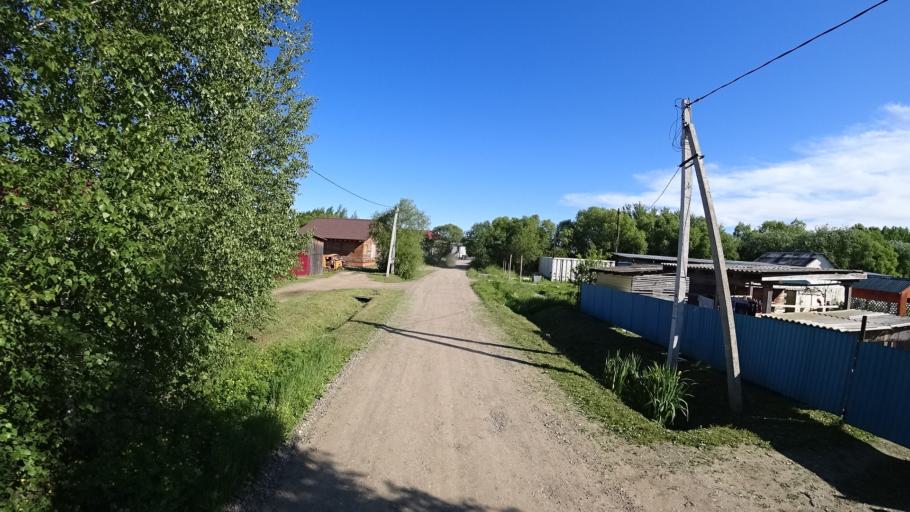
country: RU
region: Khabarovsk Krai
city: Khor
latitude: 47.8930
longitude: 134.9948
